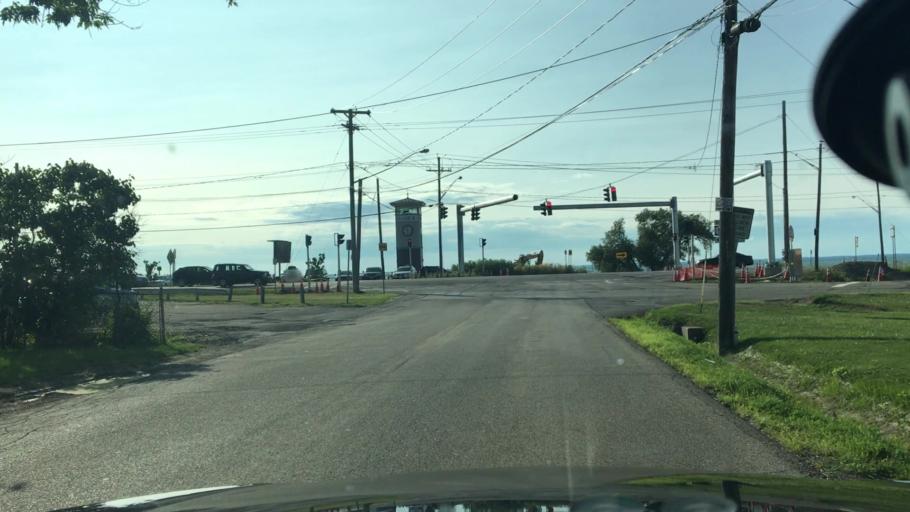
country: US
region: New York
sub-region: Erie County
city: Blasdell
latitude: 42.7734
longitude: -78.8628
